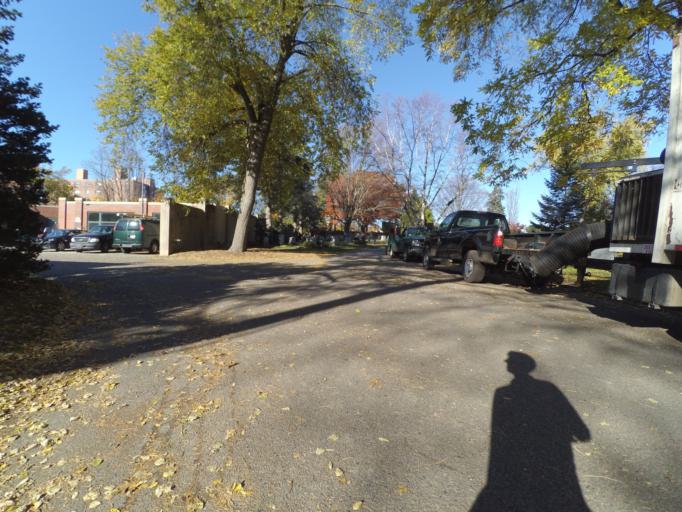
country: US
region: Massachusetts
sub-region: Middlesex County
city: Watertown
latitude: 42.3733
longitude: -71.1497
